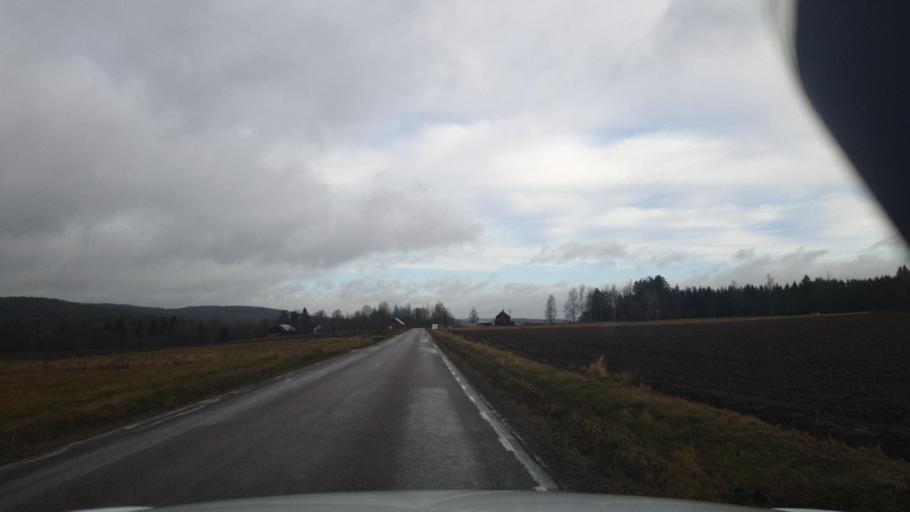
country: SE
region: Vaermland
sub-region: Eda Kommun
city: Charlottenberg
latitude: 59.7552
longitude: 12.1577
